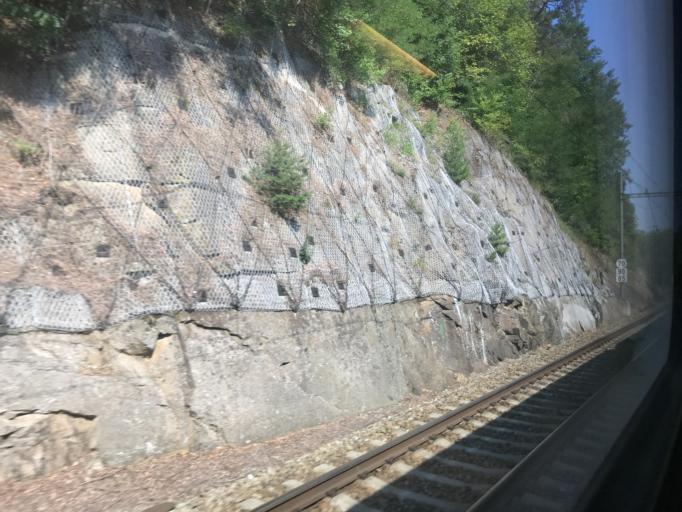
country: CZ
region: Central Bohemia
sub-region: Okres Praha-Vychod
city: Mnichovice
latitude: 49.9261
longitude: 14.7140
